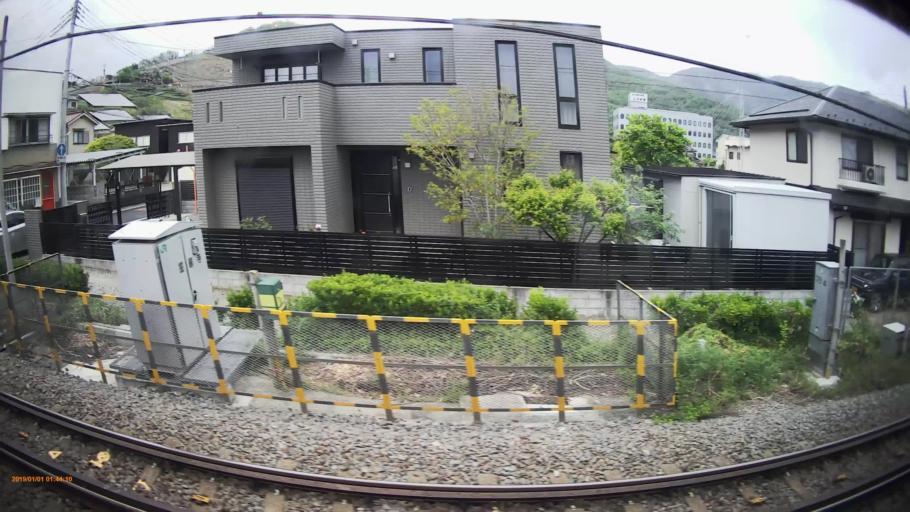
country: JP
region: Yamanashi
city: Kofu-shi
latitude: 35.6616
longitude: 138.5816
